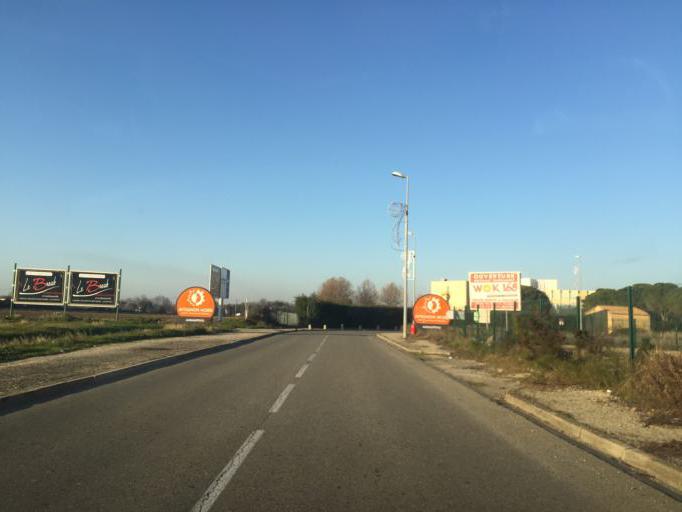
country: FR
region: Provence-Alpes-Cote d'Azur
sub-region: Departement du Vaucluse
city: Le Pontet
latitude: 43.9816
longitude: 4.8738
